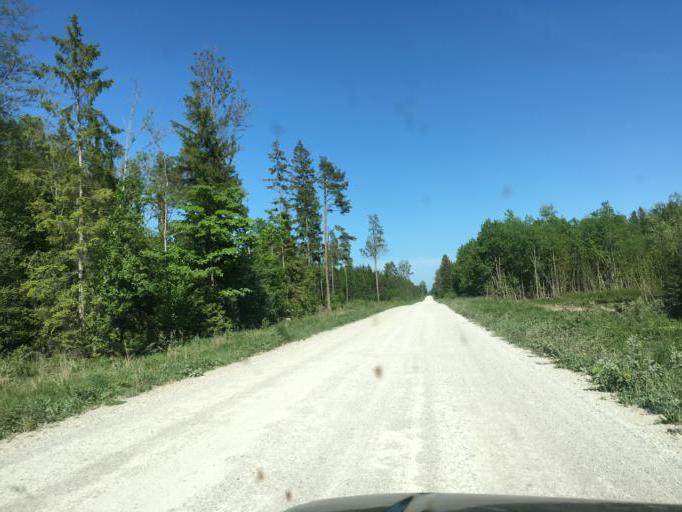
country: LV
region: Dundaga
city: Dundaga
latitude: 57.6113
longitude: 22.4840
